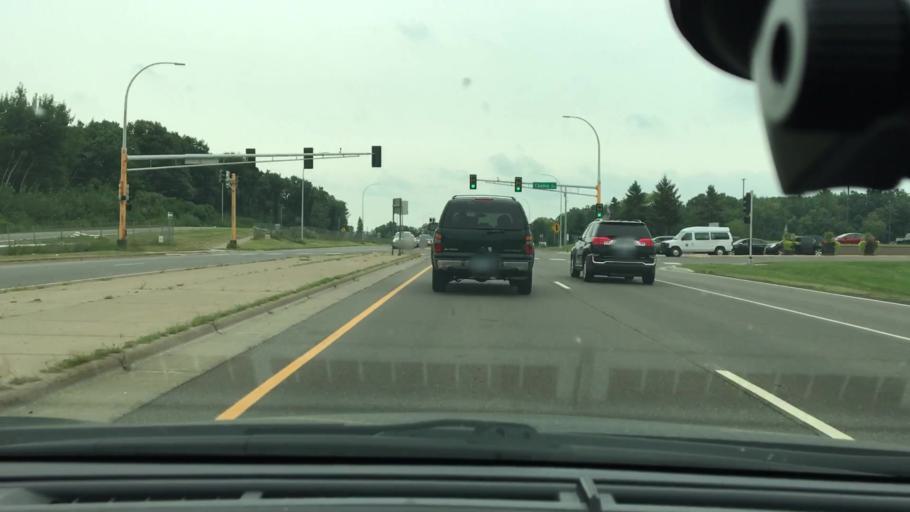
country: US
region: Minnesota
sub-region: Mille Lacs County
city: Vineland
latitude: 46.1806
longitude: -93.7566
